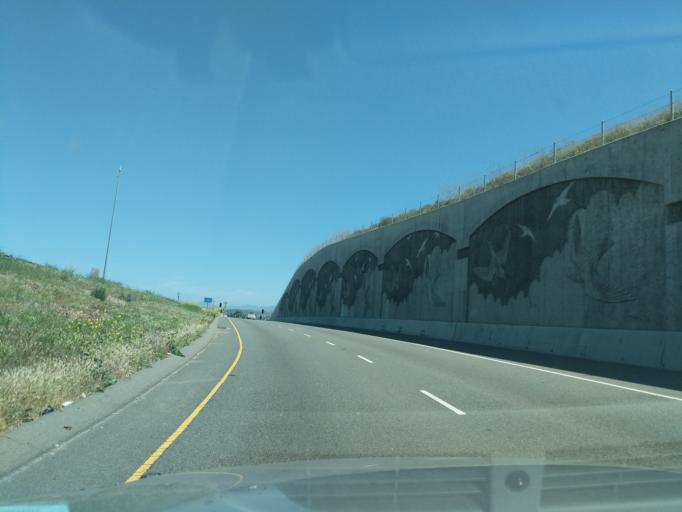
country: US
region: California
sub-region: Orange County
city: Dana Point
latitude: 33.4749
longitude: -117.6741
